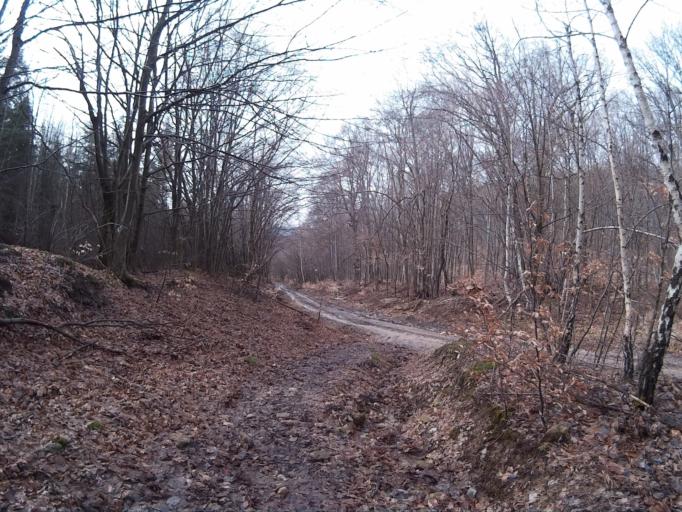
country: HU
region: Borsod-Abauj-Zemplen
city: Tolcsva
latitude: 48.4061
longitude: 21.4672
